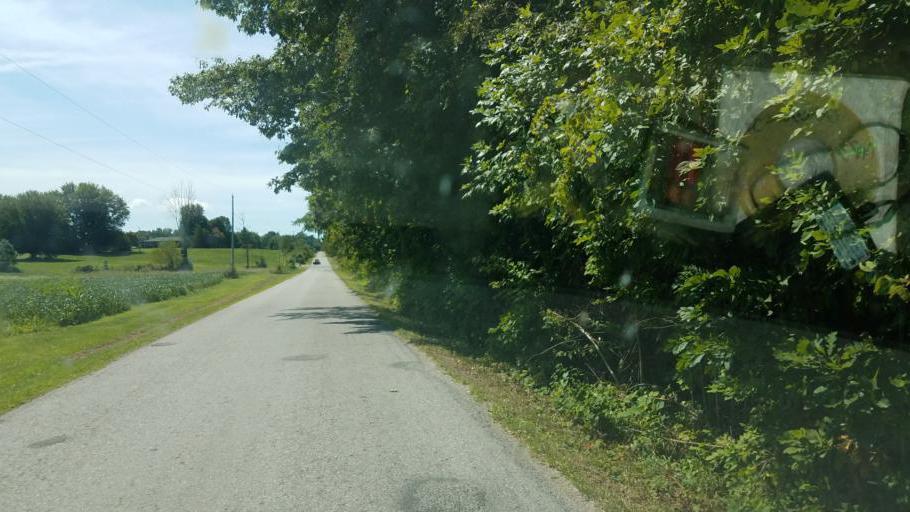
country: US
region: Ohio
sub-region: Knox County
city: Centerburg
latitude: 40.4304
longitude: -82.7379
